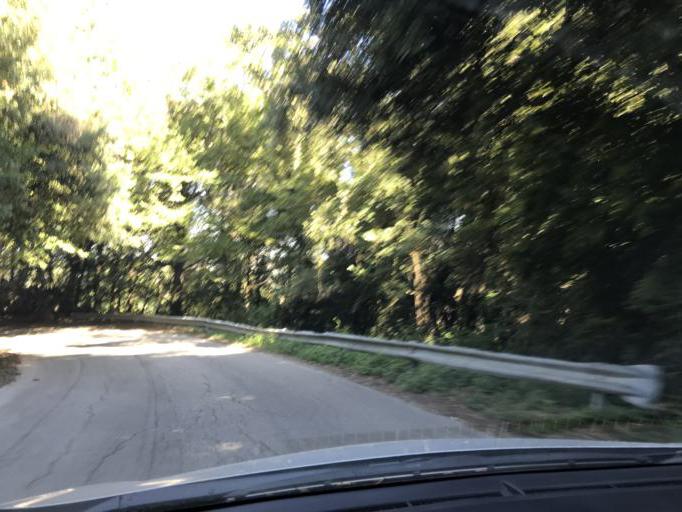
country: IT
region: Umbria
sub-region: Provincia di Terni
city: Avigliano Umbro
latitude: 42.6159
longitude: 12.4093
